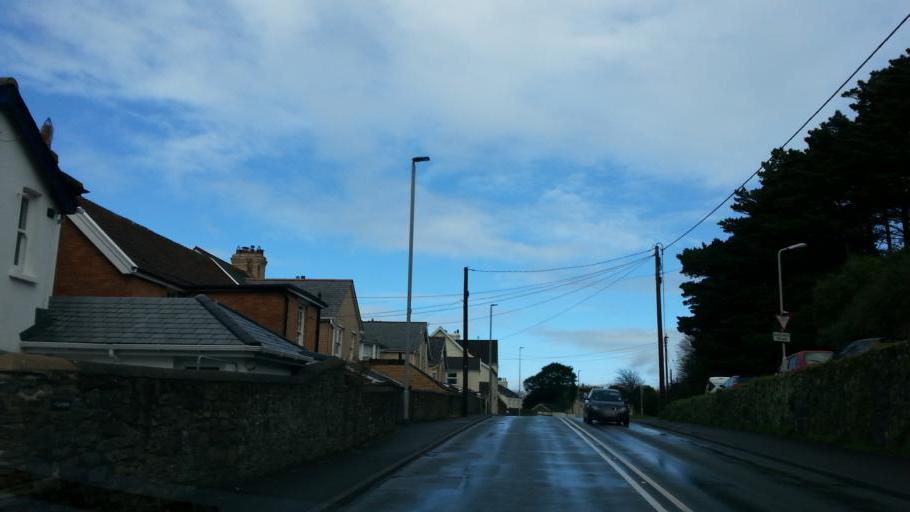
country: GB
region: England
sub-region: Devon
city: Appledore
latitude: 51.0511
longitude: -4.1786
